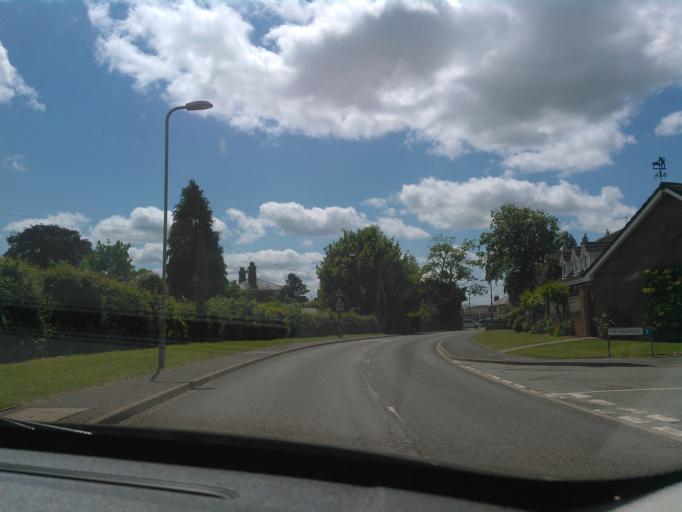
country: GB
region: England
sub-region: Shropshire
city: Wem
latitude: 52.8612
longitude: -2.7211
